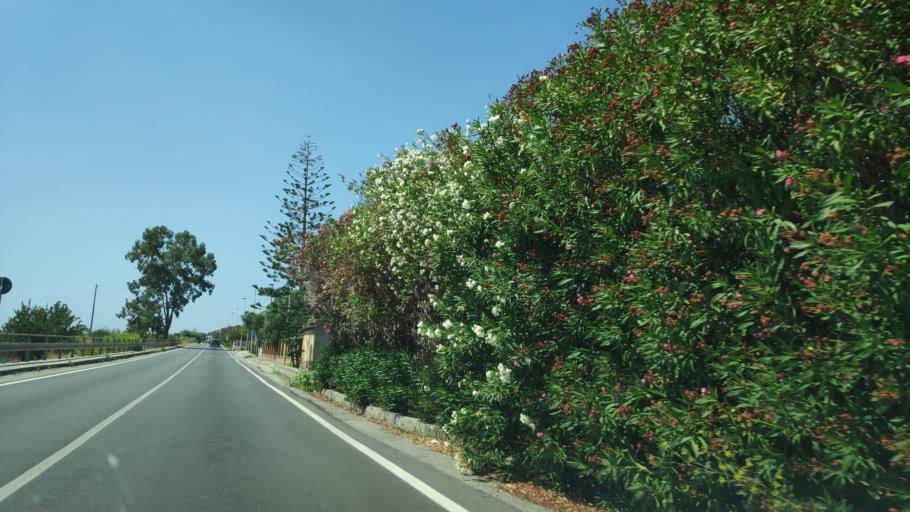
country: IT
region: Calabria
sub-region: Provincia di Reggio Calabria
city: Weather Station
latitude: 37.9554
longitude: 16.0932
